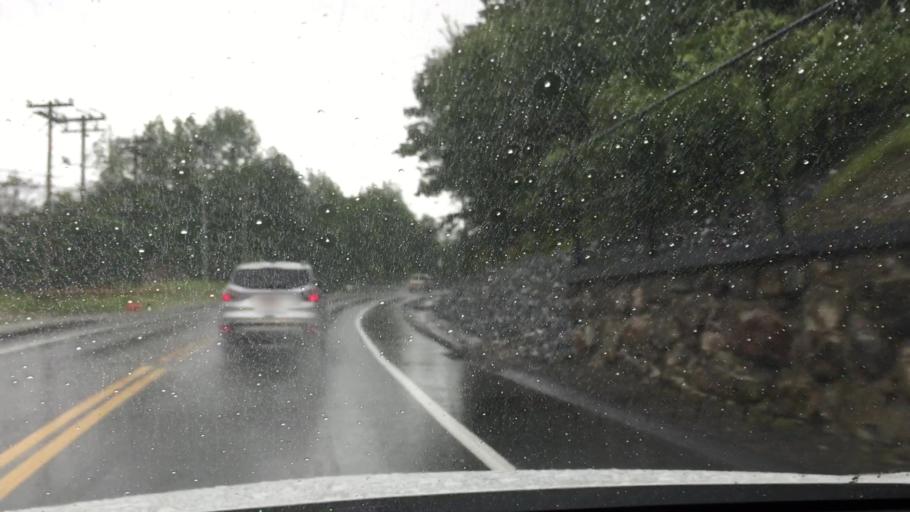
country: US
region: Massachusetts
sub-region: Berkshire County
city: Dalton
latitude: 42.4706
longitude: -73.1672
